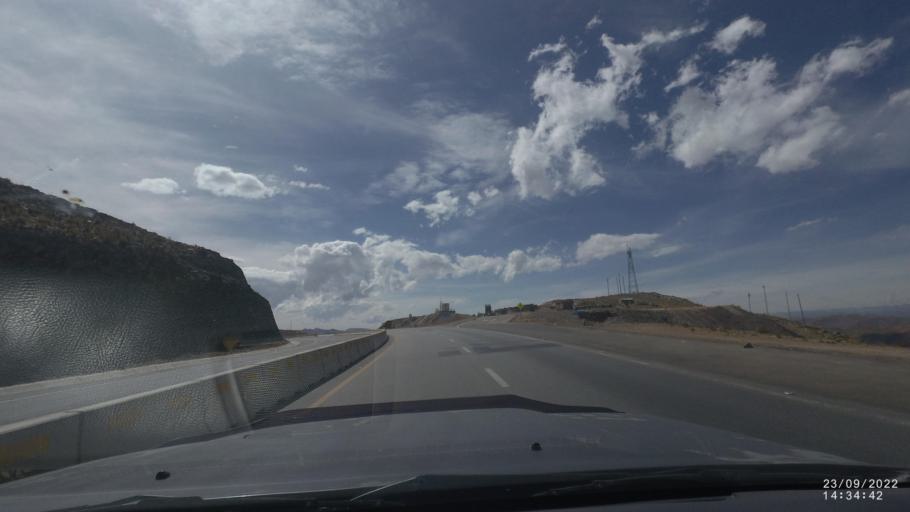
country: BO
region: Cochabamba
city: Colchani
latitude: -17.6653
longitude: -66.8197
